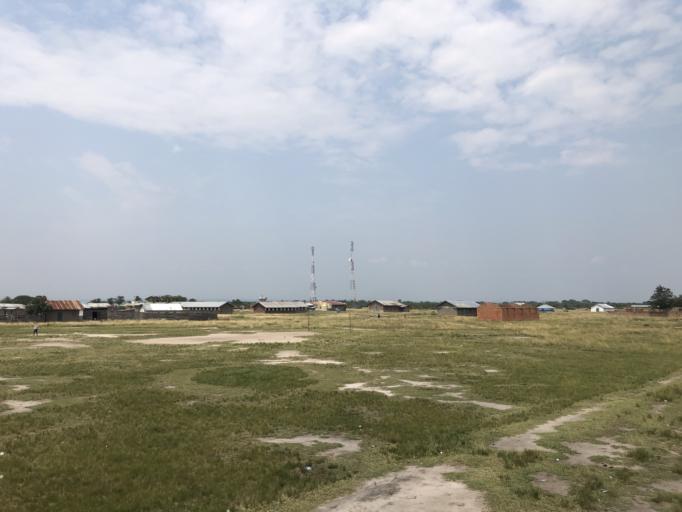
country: UG
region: Western Region
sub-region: Rubirizi District
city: Rubirizi
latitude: -0.4109
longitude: 29.7730
